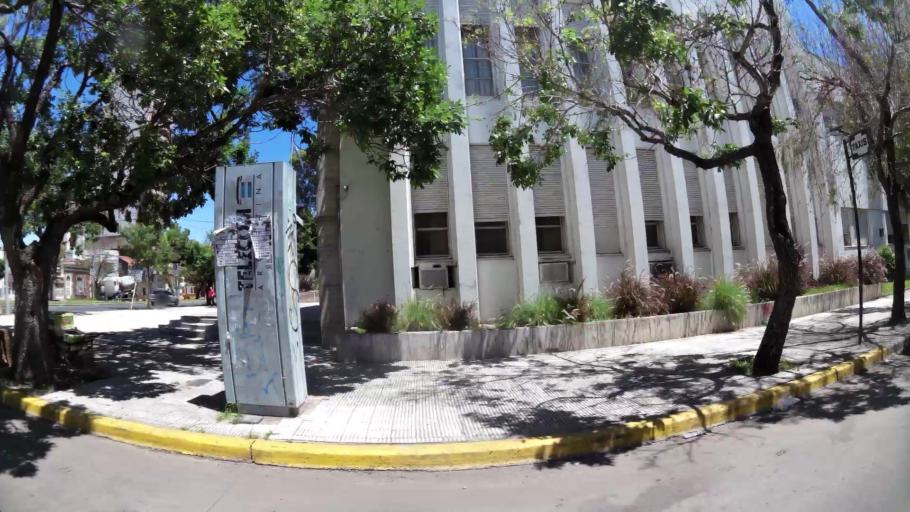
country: AR
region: Santa Fe
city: Santa Fe de la Vera Cruz
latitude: -31.6340
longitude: -60.7098
